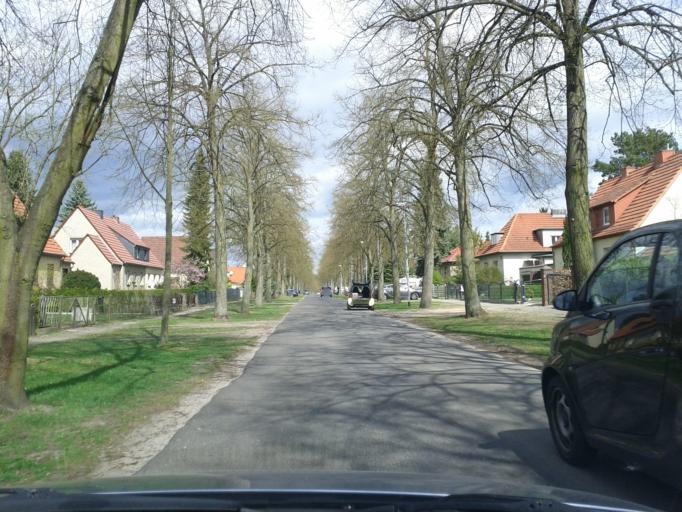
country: DE
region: Brandenburg
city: Schoneiche
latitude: 52.4711
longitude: 13.7015
